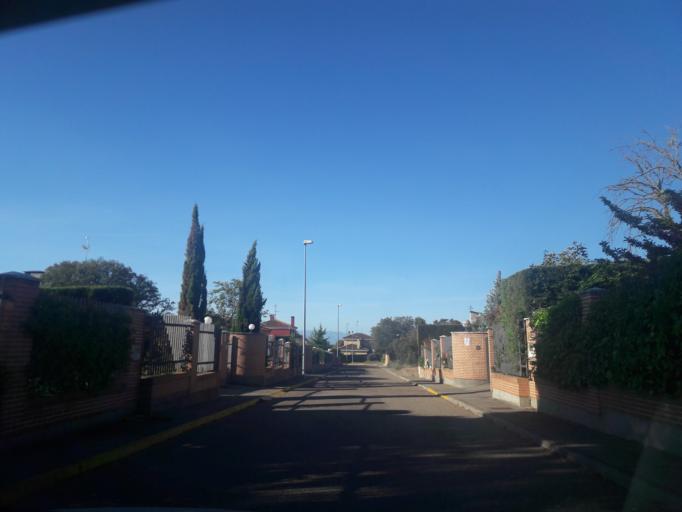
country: ES
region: Castille and Leon
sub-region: Provincia de Salamanca
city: Martinamor
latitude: 40.8077
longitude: -5.6335
